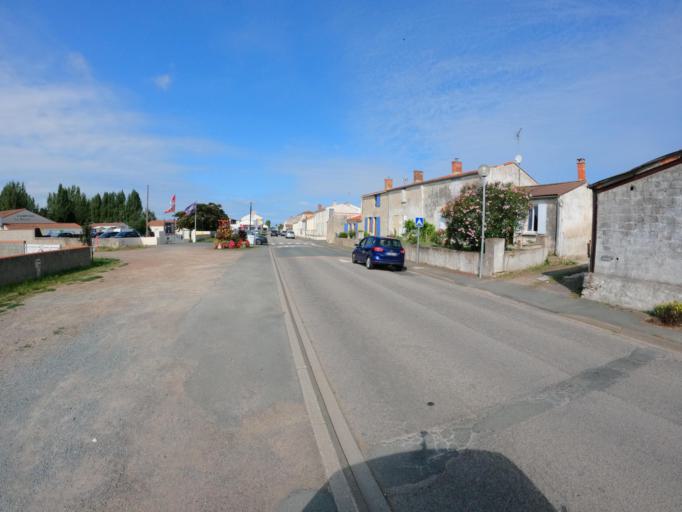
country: FR
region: Pays de la Loire
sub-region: Departement de la Vendee
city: Triaize
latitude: 46.3495
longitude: -1.2541
